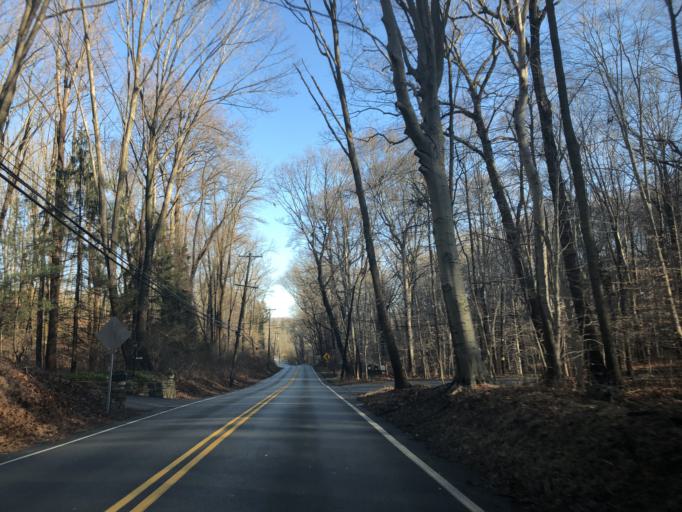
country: US
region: Pennsylvania
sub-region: Delaware County
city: Chester Heights
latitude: 39.9046
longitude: -75.4863
